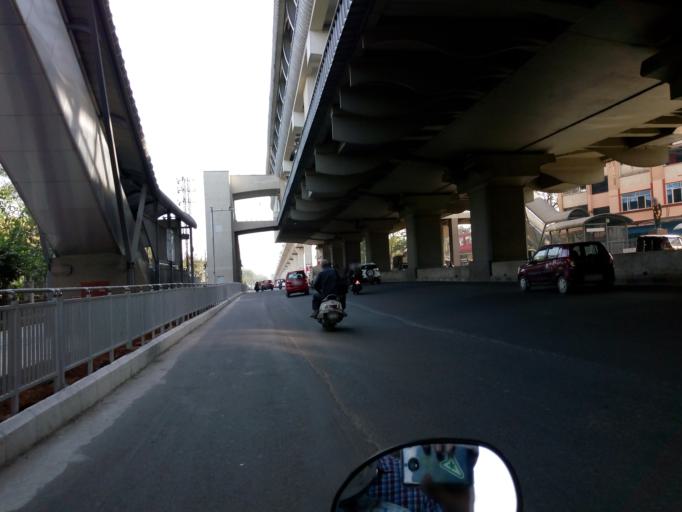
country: IN
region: Telangana
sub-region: Rangareddi
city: Uppal Kalan
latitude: 17.4151
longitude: 78.5461
